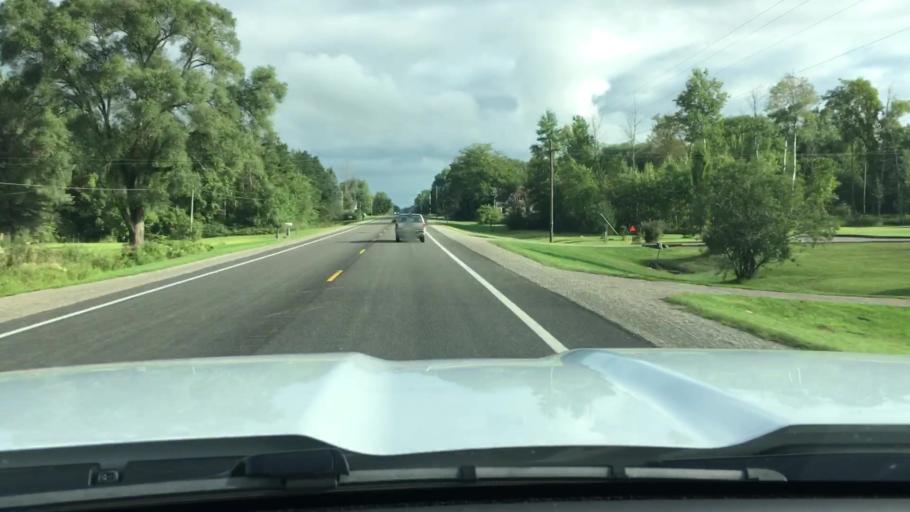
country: US
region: Michigan
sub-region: Tuscola County
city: Caro
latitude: 43.4397
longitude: -83.3850
